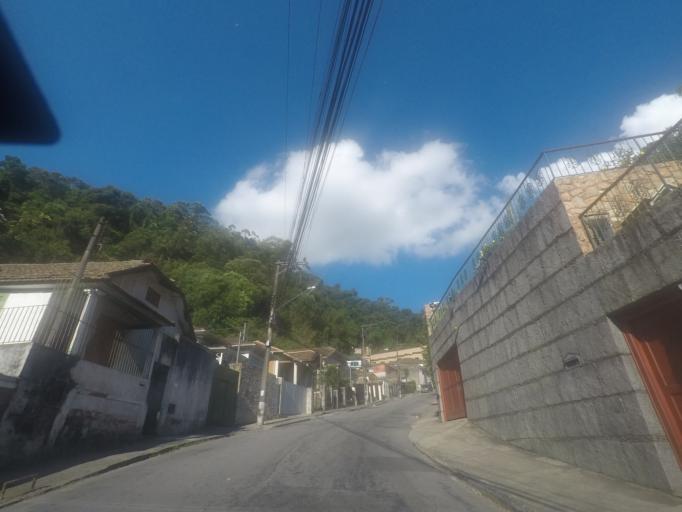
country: BR
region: Rio de Janeiro
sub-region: Petropolis
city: Petropolis
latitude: -22.5067
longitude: -43.1641
